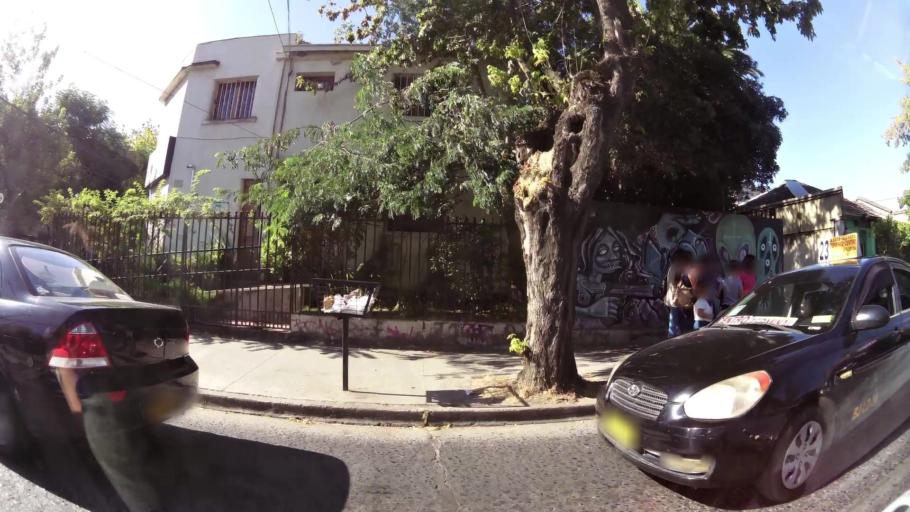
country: CL
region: Maule
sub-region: Provincia de Talca
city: Talca
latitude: -35.4250
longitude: -71.6608
